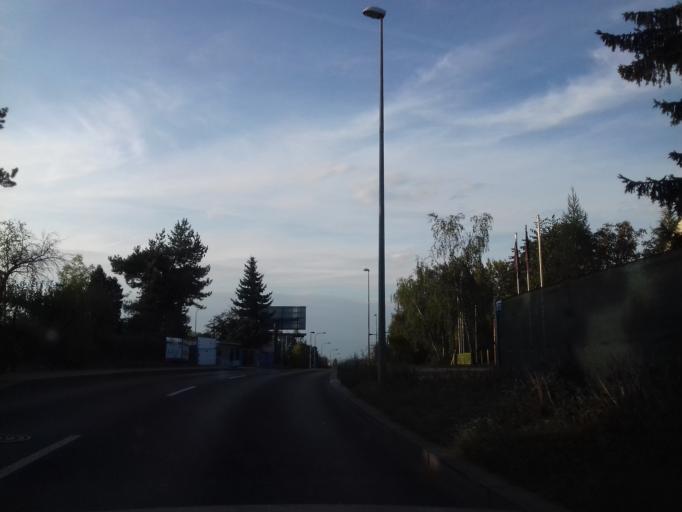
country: CZ
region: Praha
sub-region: Praha 4
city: Hodkovicky
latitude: 50.0154
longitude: 14.4554
